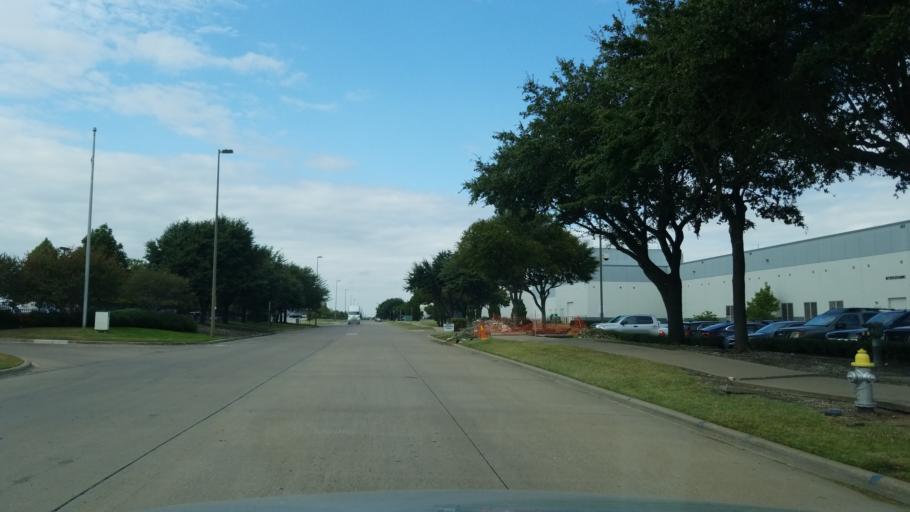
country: US
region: Texas
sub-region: Dallas County
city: Garland
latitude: 32.8891
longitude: -96.6841
